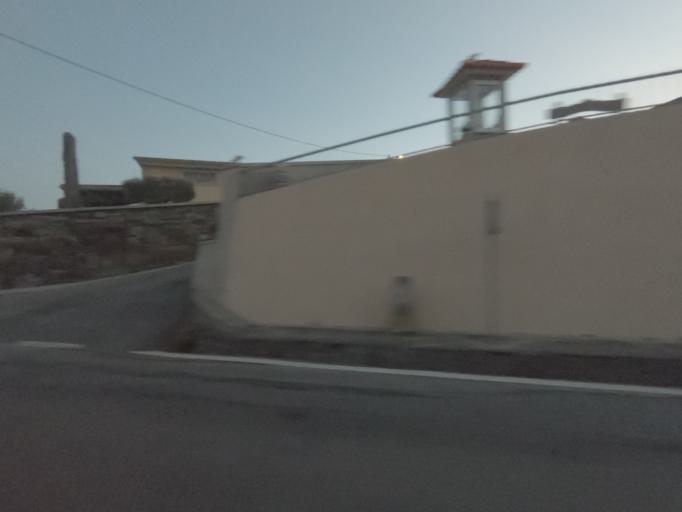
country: PT
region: Vila Real
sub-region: Sabrosa
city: Vilela
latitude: 41.2375
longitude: -7.6831
